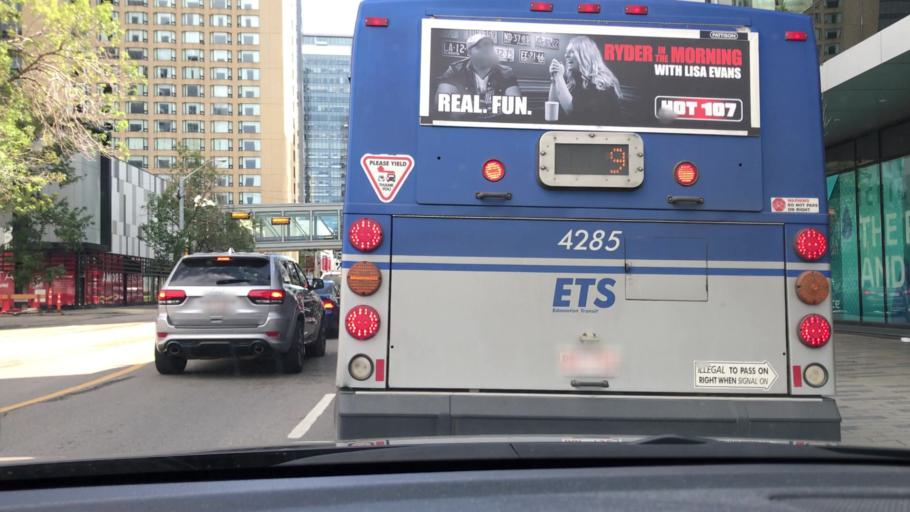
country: CA
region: Alberta
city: Edmonton
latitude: 53.5462
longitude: -113.4938
